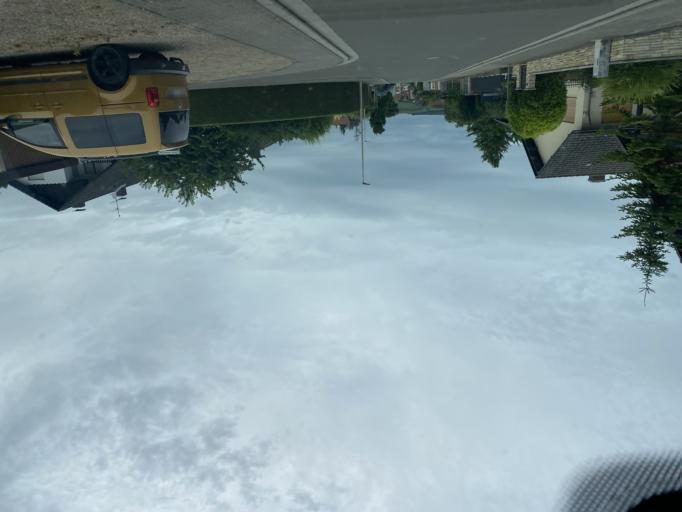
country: DE
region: Rheinland-Pfalz
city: Sprendlingen
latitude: 49.8572
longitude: 7.9903
